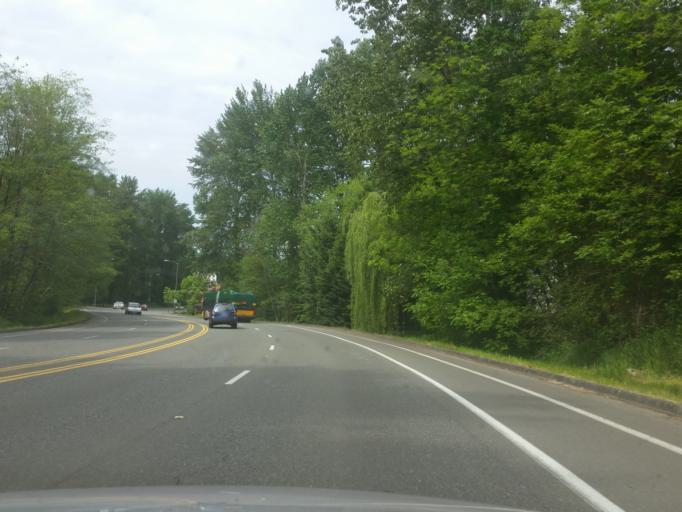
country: US
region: Washington
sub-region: King County
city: Kirkland
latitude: 47.7011
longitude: -122.2088
